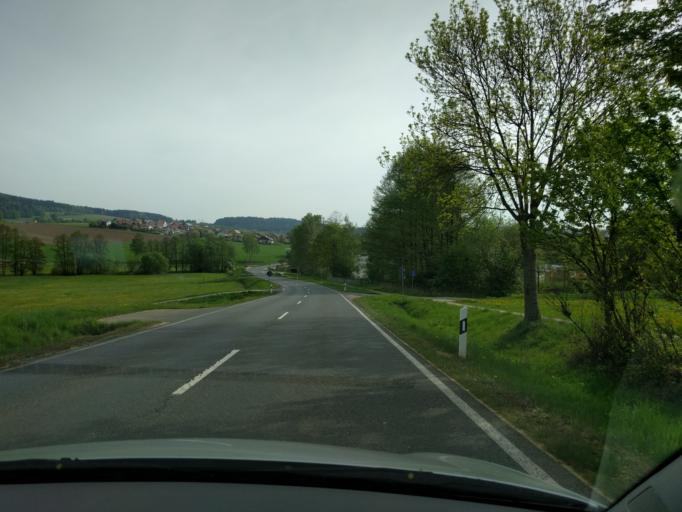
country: DE
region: Bavaria
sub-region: Upper Palatinate
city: Falkenstein
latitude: 49.1035
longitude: 12.4959
